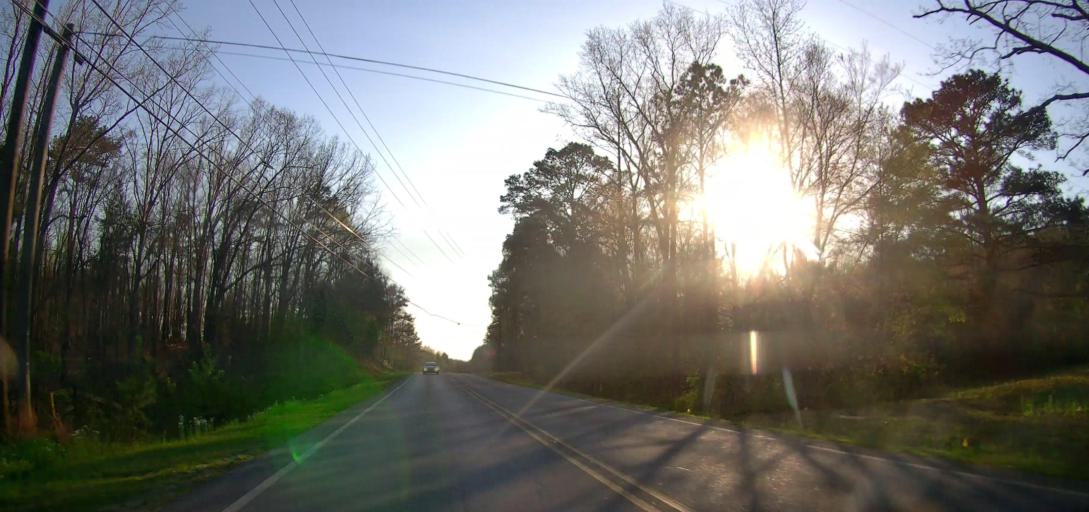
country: US
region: Alabama
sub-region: Shelby County
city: Pelham
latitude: 33.2856
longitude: -86.7687
